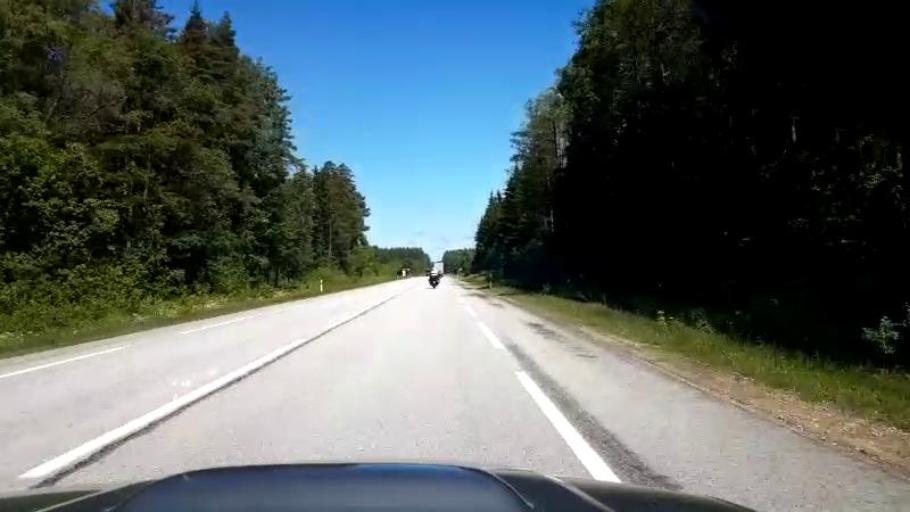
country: LV
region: Saulkrastu
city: Saulkrasti
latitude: 57.4238
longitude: 24.4290
